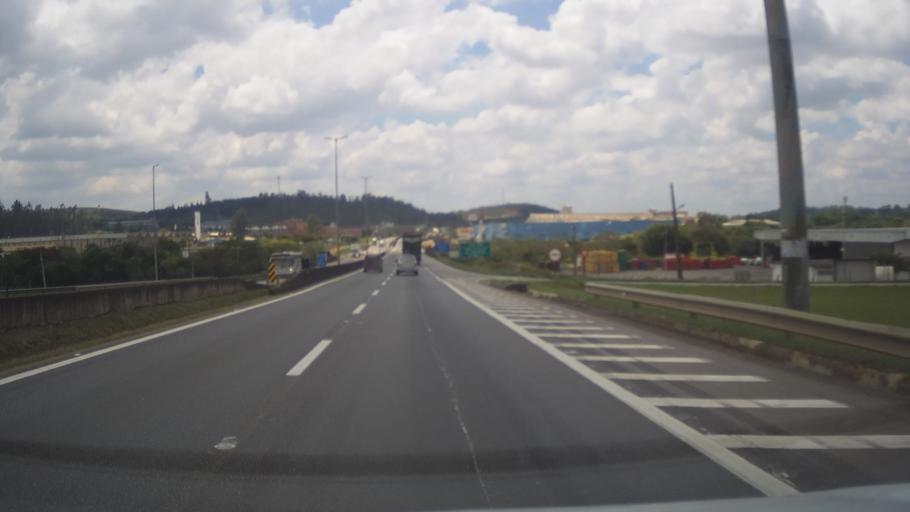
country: BR
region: Minas Gerais
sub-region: Tres Coracoes
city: Tres Coracoes
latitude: -21.6731
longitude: -45.3354
